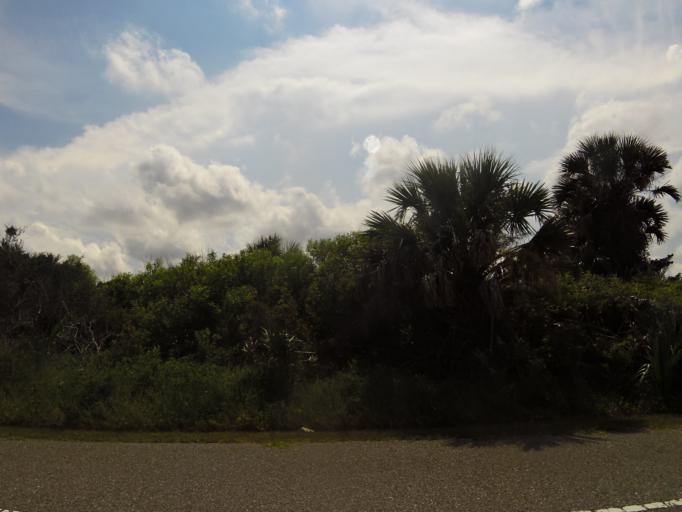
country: US
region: Florida
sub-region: Duval County
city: Atlantic Beach
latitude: 30.4553
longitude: -81.4135
